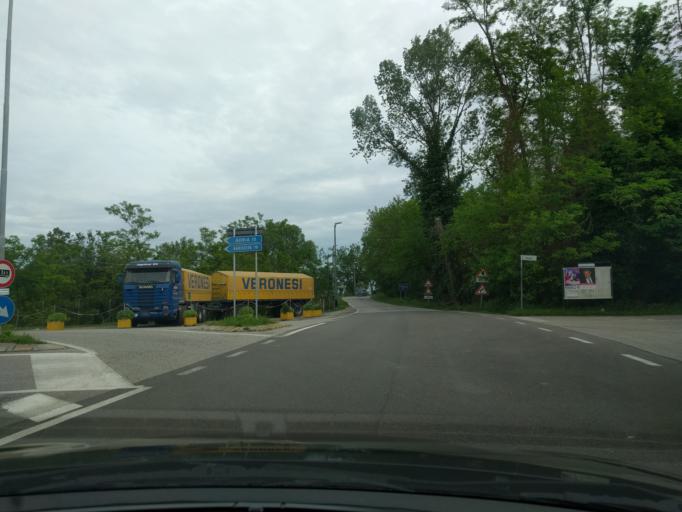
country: IT
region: Veneto
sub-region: Provincia di Rovigo
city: Ceregnano
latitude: 45.0386
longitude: 11.8857
